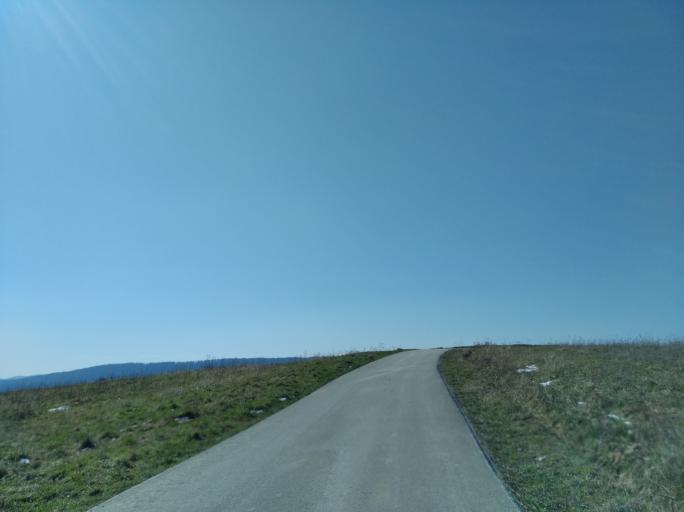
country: PL
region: Subcarpathian Voivodeship
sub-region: Powiat strzyzowski
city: Strzyzow
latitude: 49.8549
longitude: 21.8151
